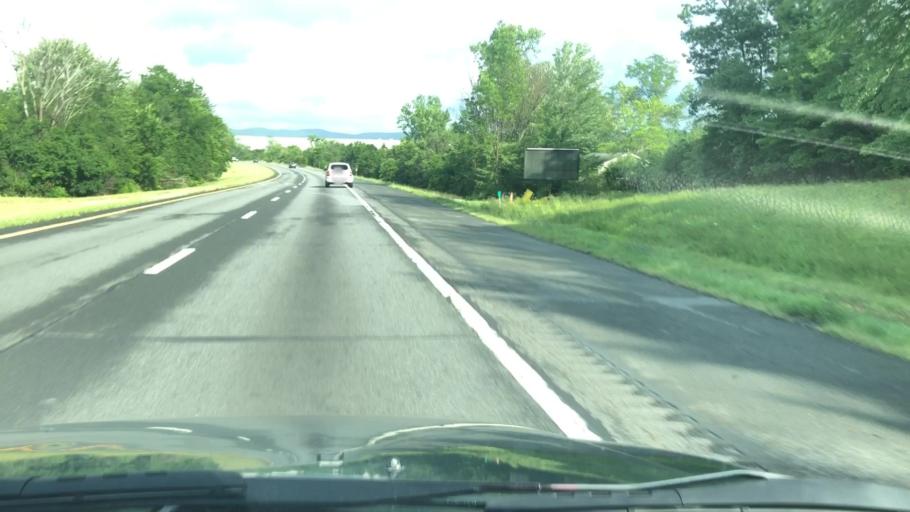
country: US
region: New York
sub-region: Orange County
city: Orange Lake
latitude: 41.5177
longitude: -74.0884
